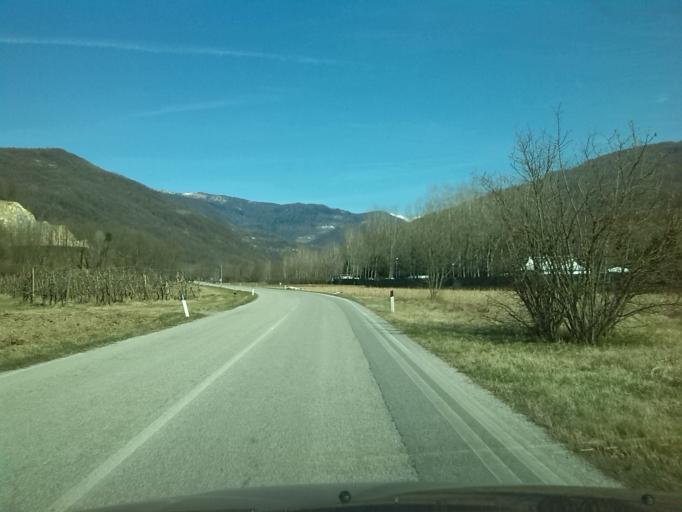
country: IT
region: Friuli Venezia Giulia
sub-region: Provincia di Udine
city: Merso di Sopra
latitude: 46.1332
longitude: 13.5027
